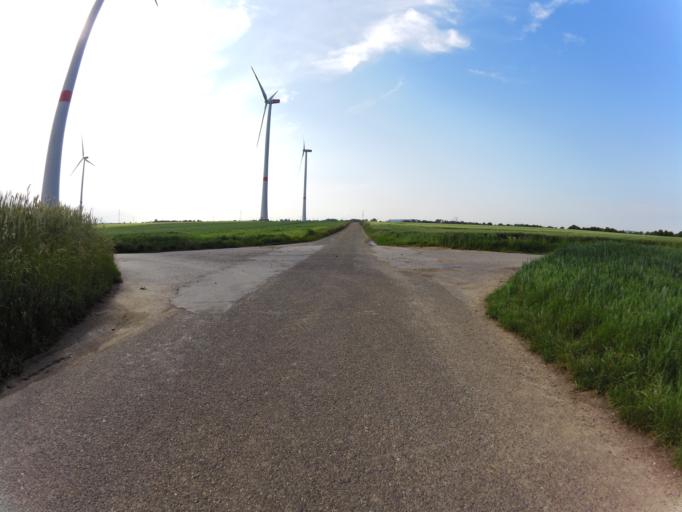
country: DE
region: North Rhine-Westphalia
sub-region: Regierungsbezirk Koln
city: Linnich
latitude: 50.9782
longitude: 6.2040
